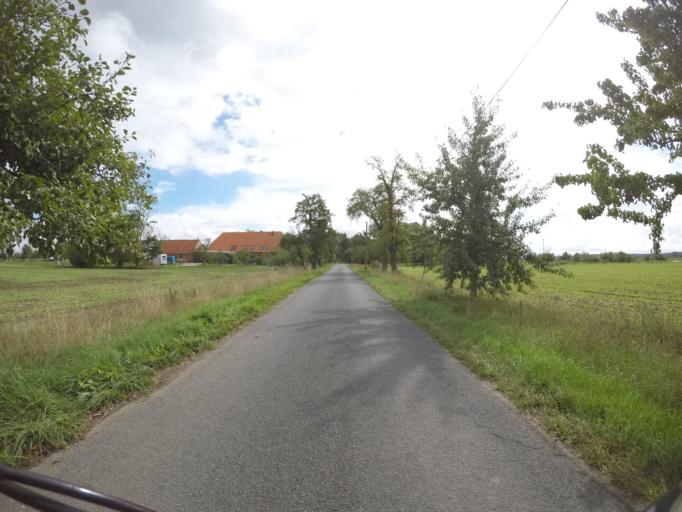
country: DE
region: Lower Saxony
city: Neu Darchau
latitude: 53.2588
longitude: 10.8588
